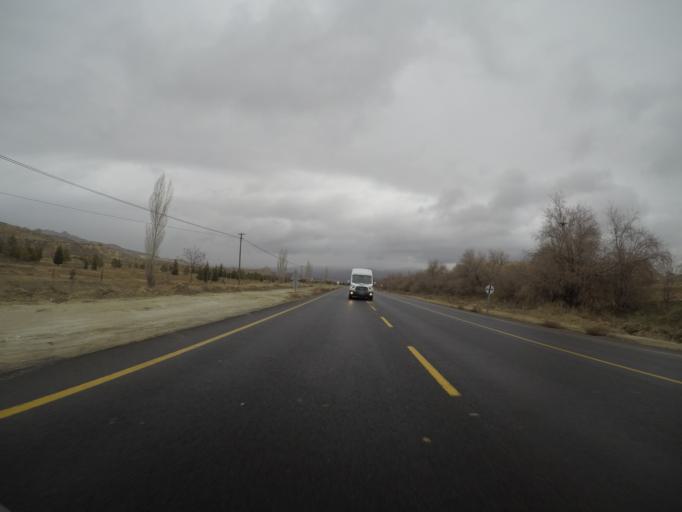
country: TR
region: Nevsehir
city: Goereme
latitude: 38.6749
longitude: 34.8391
